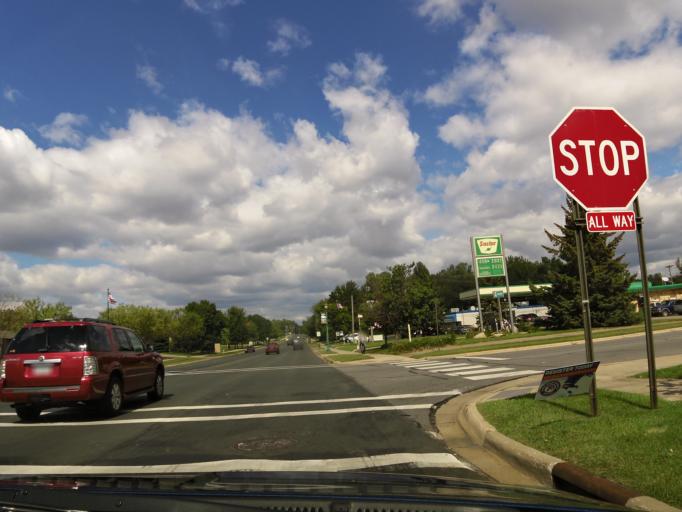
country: US
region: Minnesota
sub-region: Dakota County
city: Inver Grove Heights
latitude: 44.8551
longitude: -93.0449
